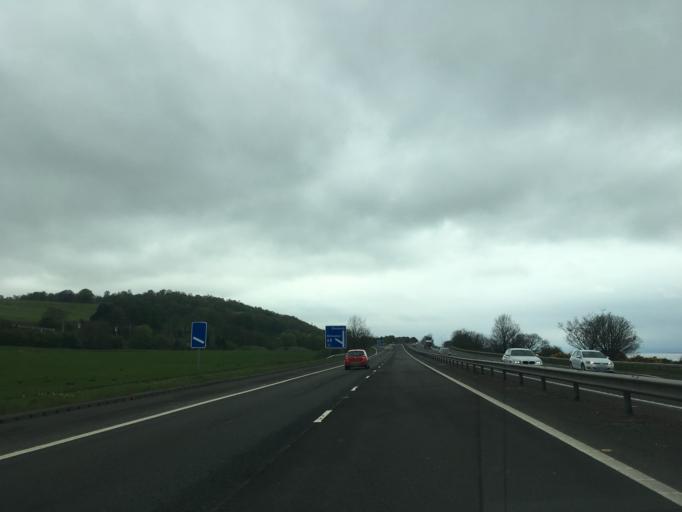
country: GB
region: Scotland
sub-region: West Dunbartonshire
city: Dumbarton
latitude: 55.9232
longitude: -4.5465
